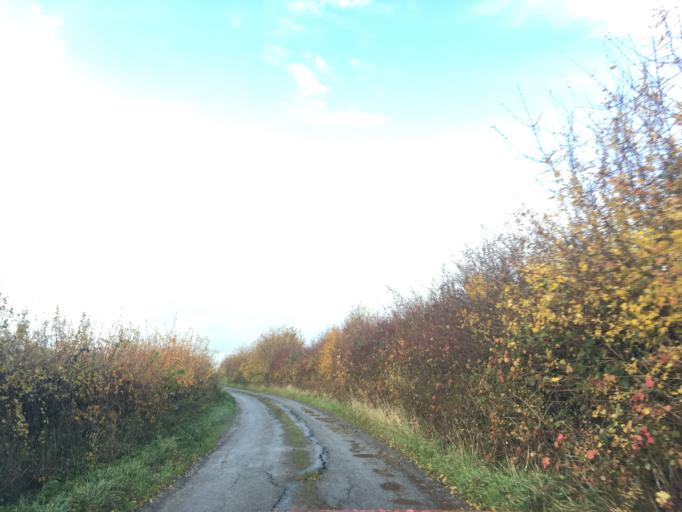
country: GB
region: England
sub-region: South Gloucestershire
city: Pucklechurch
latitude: 51.4537
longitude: -2.4067
